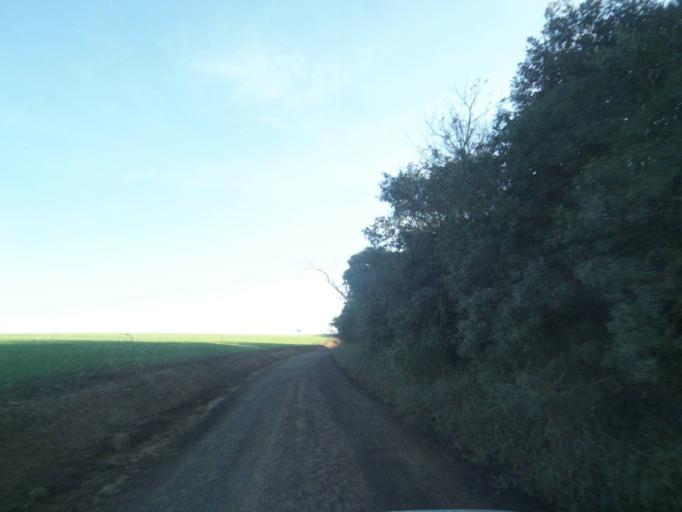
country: BR
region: Parana
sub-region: Telemaco Borba
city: Telemaco Borba
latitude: -24.4316
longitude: -50.5987
